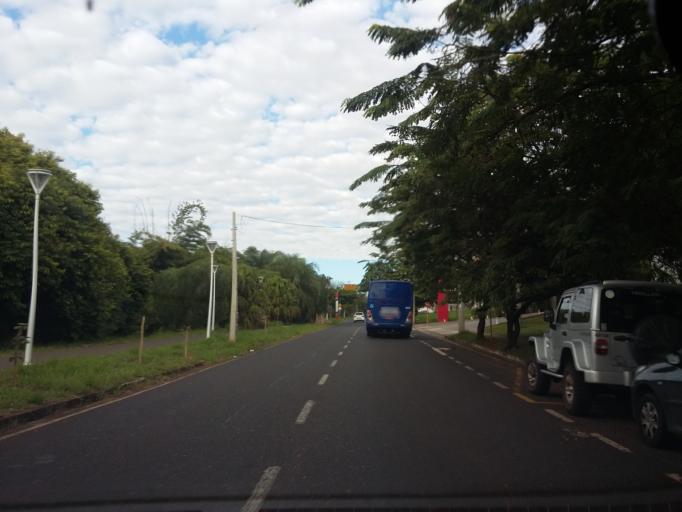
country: BR
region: Sao Paulo
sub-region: Sao Jose Do Rio Preto
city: Sao Jose do Rio Preto
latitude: -20.8336
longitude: -49.4065
